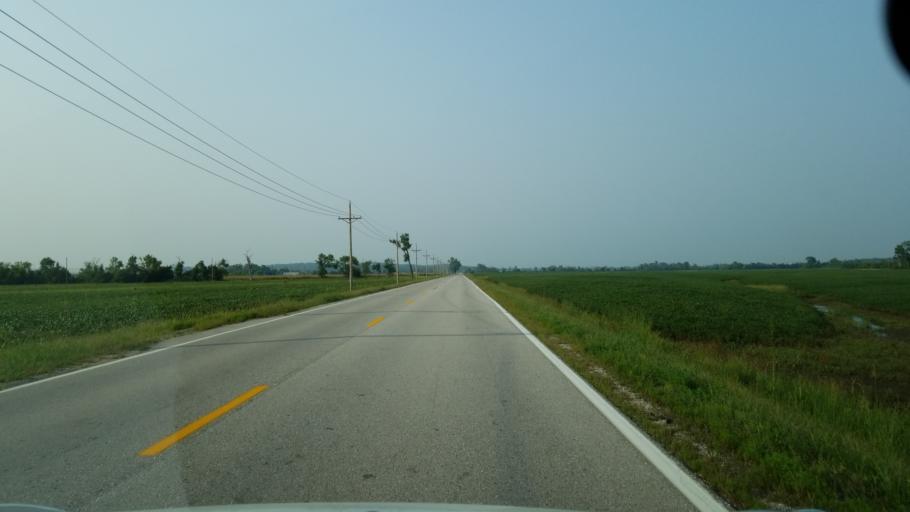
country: US
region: Nebraska
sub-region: Sarpy County
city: Offutt Air Force Base
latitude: 41.0942
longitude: -95.8898
